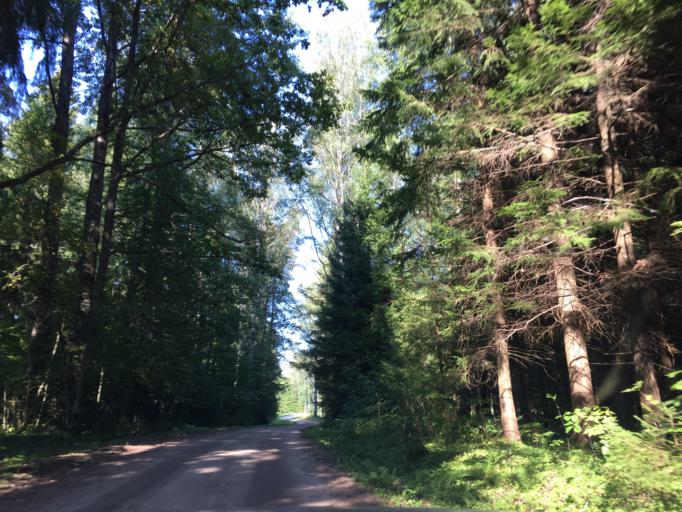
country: LV
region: Limbazu Rajons
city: Limbazi
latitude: 57.5566
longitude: 24.7826
